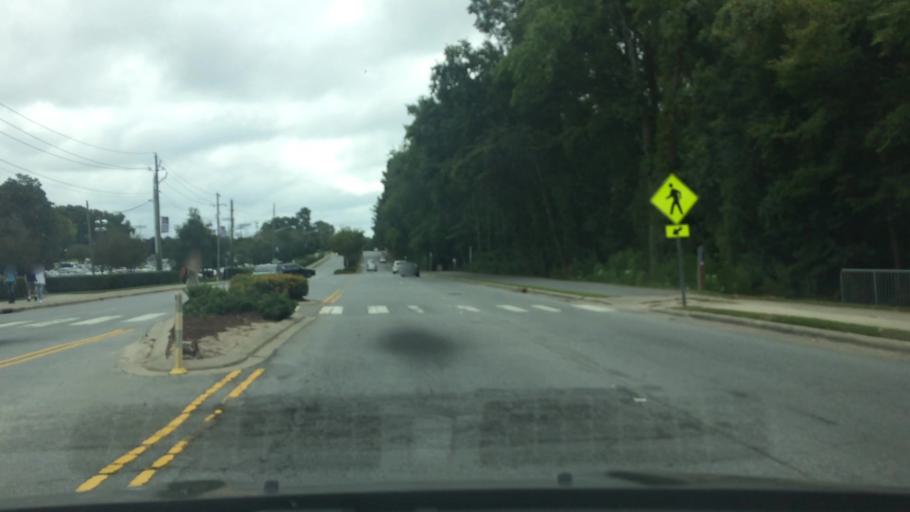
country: US
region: North Carolina
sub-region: Pitt County
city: Greenville
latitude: 35.5994
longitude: -77.3706
